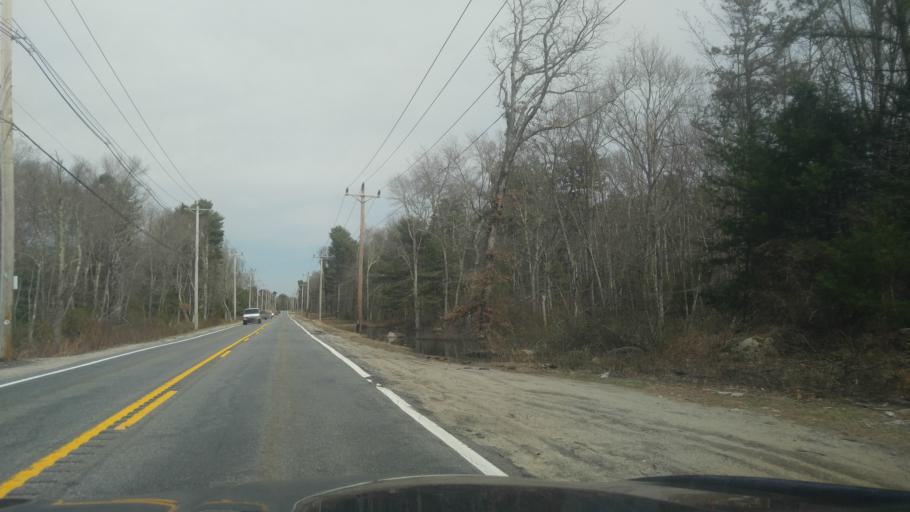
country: US
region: Rhode Island
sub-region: Kent County
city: West Warwick
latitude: 41.6510
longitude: -71.5685
